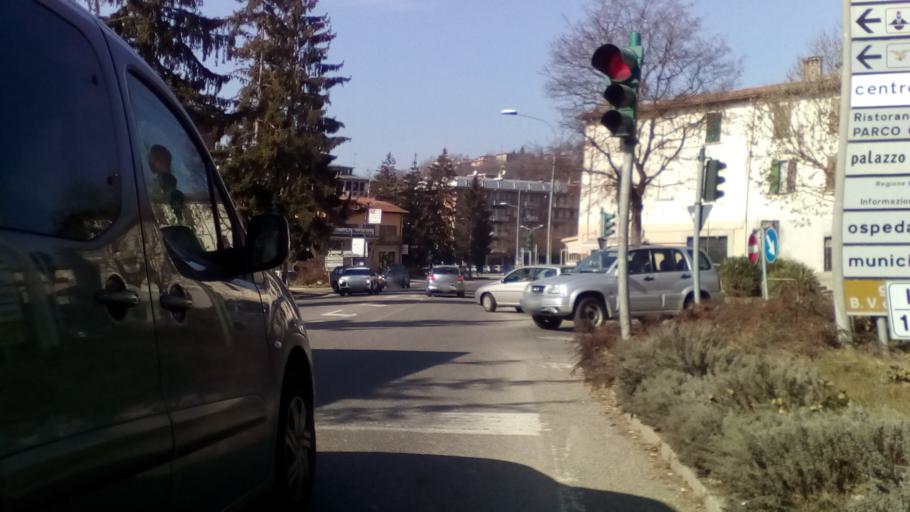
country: IT
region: Emilia-Romagna
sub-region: Provincia di Modena
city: Pavullo nel Frignano
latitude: 44.3309
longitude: 10.8346
